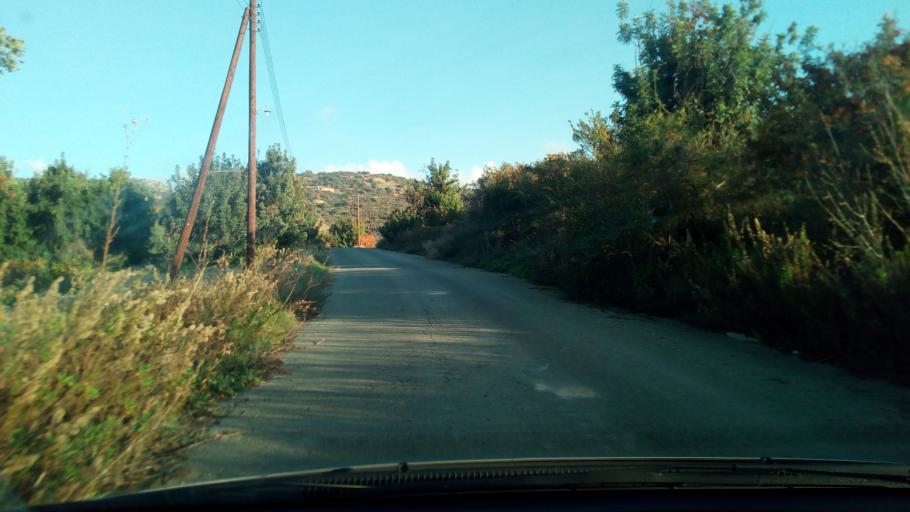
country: CY
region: Pafos
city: Polis
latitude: 34.9855
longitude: 32.4763
